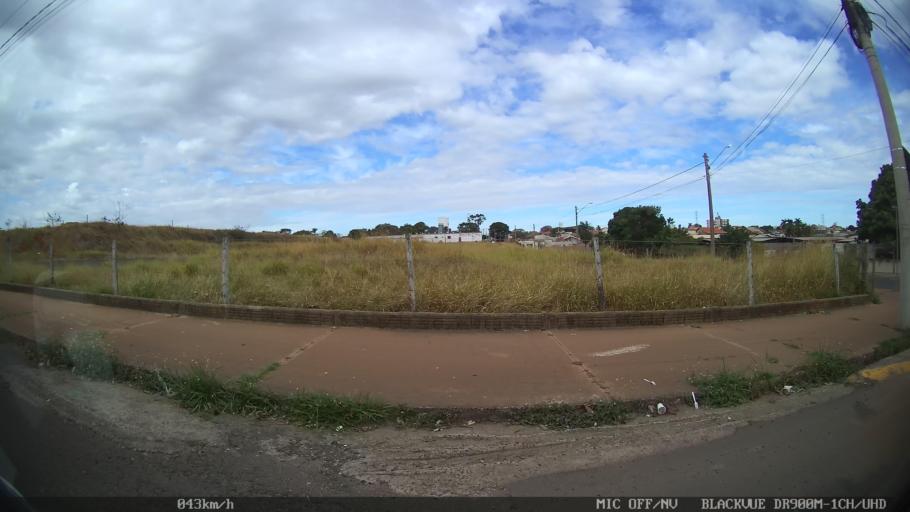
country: BR
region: Sao Paulo
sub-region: Sao Jose Do Rio Preto
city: Sao Jose do Rio Preto
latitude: -20.8103
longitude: -49.4968
